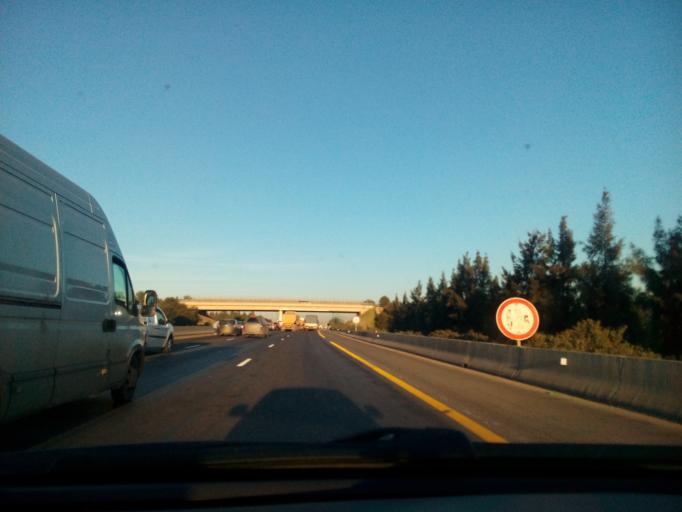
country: DZ
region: Relizane
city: Oued Rhiou
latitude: 35.9713
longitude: 0.9037
